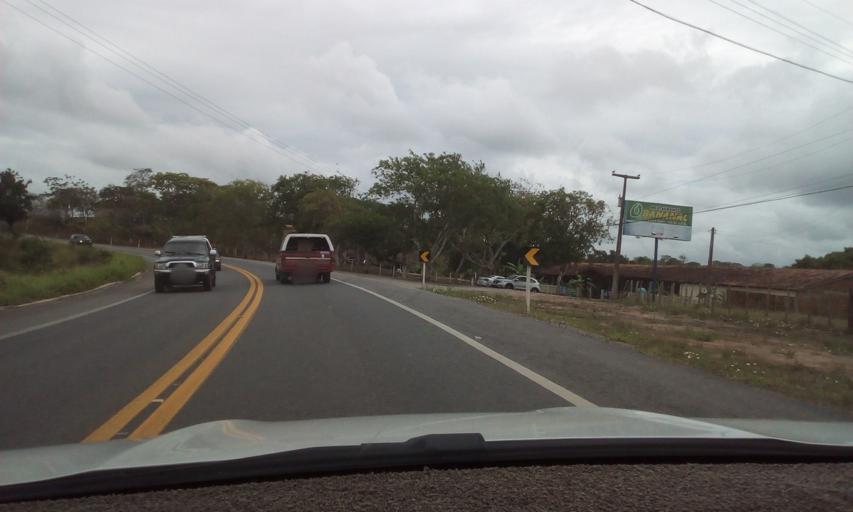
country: BR
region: Paraiba
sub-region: Lagoa Seca
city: Lagoa Seca
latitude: -7.1759
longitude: -35.8603
